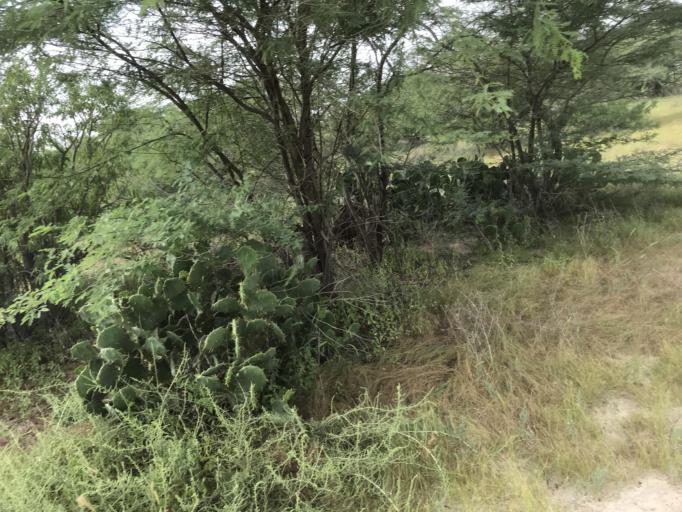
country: SN
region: Saint-Louis
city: Saint-Louis
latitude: 15.9273
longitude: -16.4655
